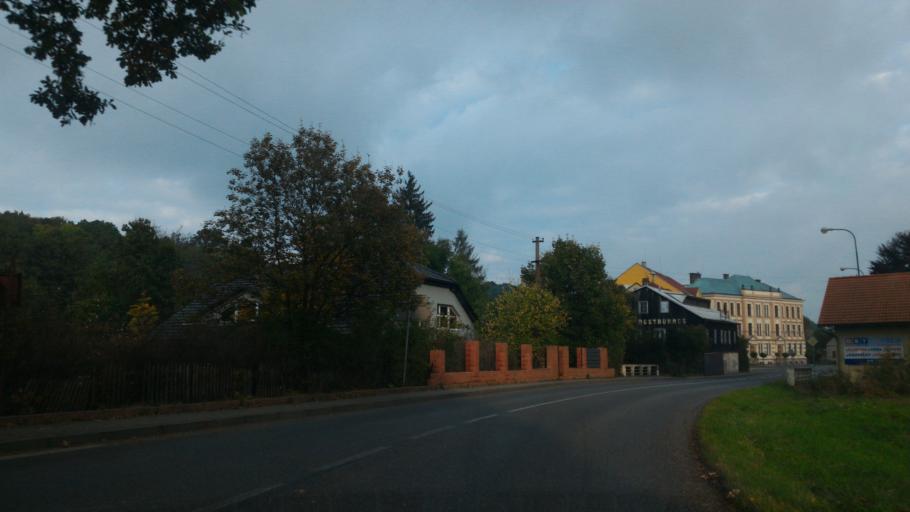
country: CZ
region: Ustecky
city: Dolni Podluzi
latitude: 50.8797
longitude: 14.5932
